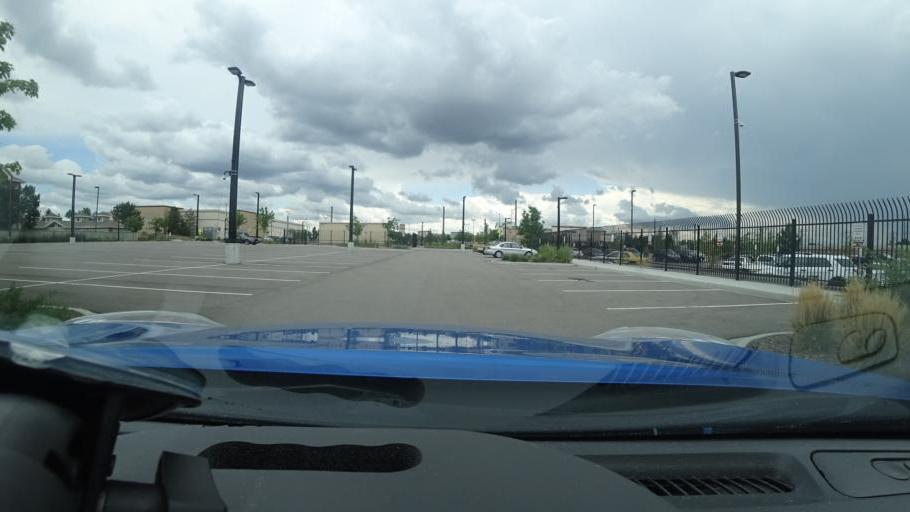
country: US
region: Colorado
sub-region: Adams County
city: Aurora
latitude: 39.7174
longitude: -104.8248
